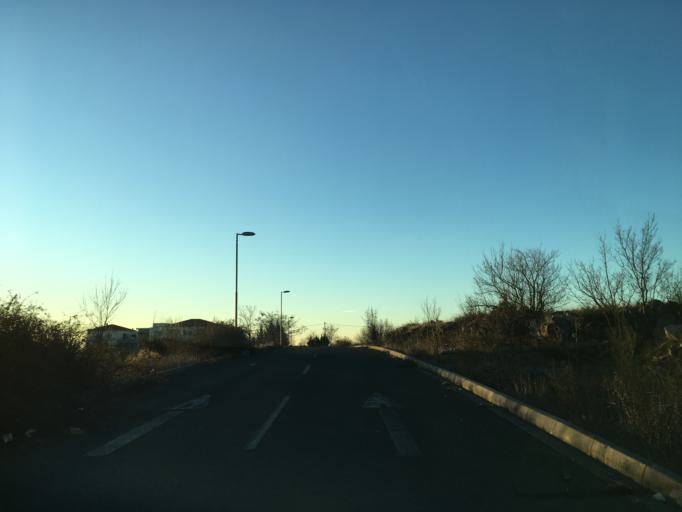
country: GR
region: West Macedonia
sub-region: Nomos Kozanis
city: Kozani
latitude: 40.2740
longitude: 21.7552
